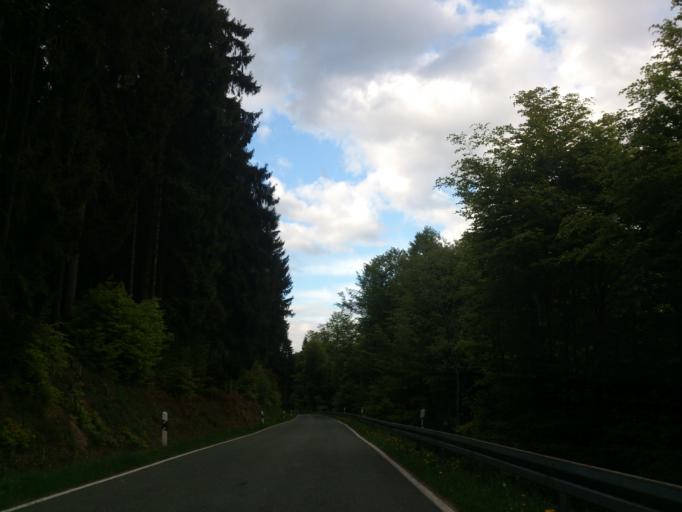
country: DE
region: North Rhine-Westphalia
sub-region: Regierungsbezirk Detmold
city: Willebadessen
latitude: 51.6096
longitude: 9.0008
